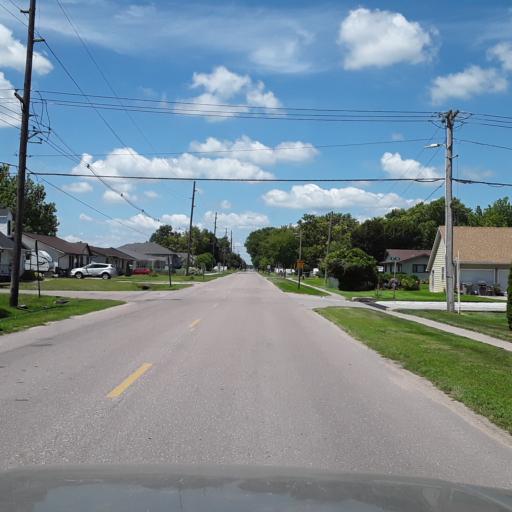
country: US
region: Nebraska
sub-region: Merrick County
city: Central City
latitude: 41.1048
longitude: -98.0035
